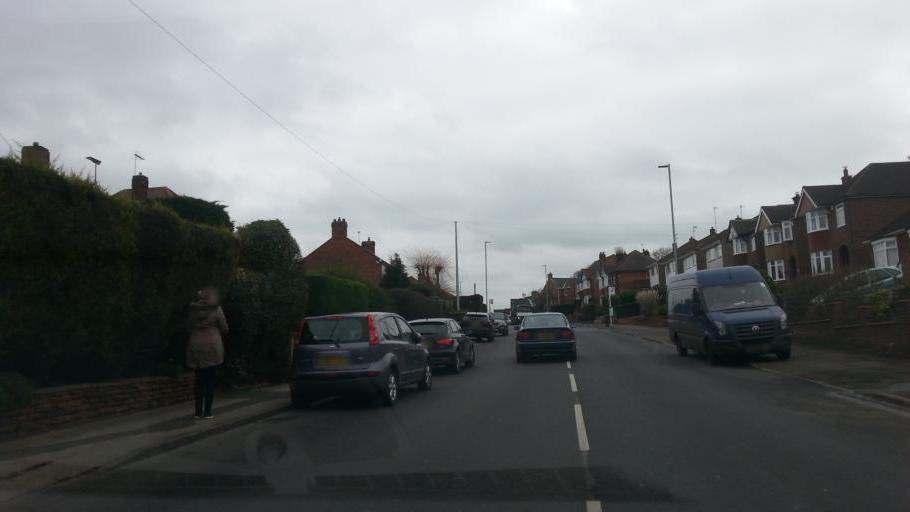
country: GB
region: England
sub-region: Nottinghamshire
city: Kimberley
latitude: 52.9962
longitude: -1.2526
